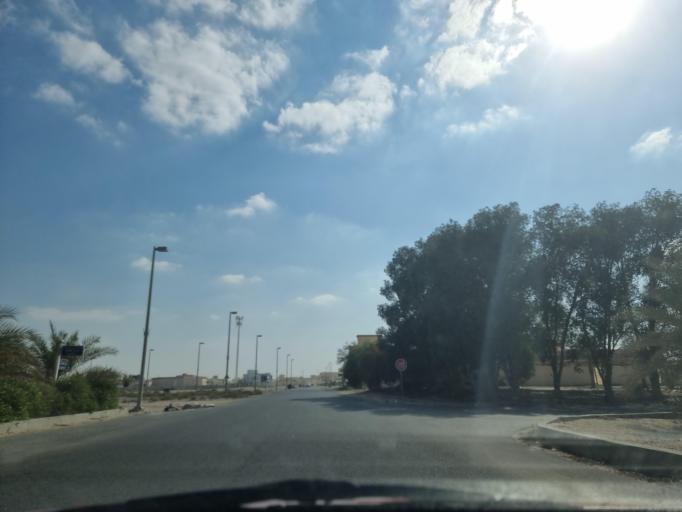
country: AE
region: Abu Dhabi
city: Abu Dhabi
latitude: 24.4018
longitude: 54.7404
